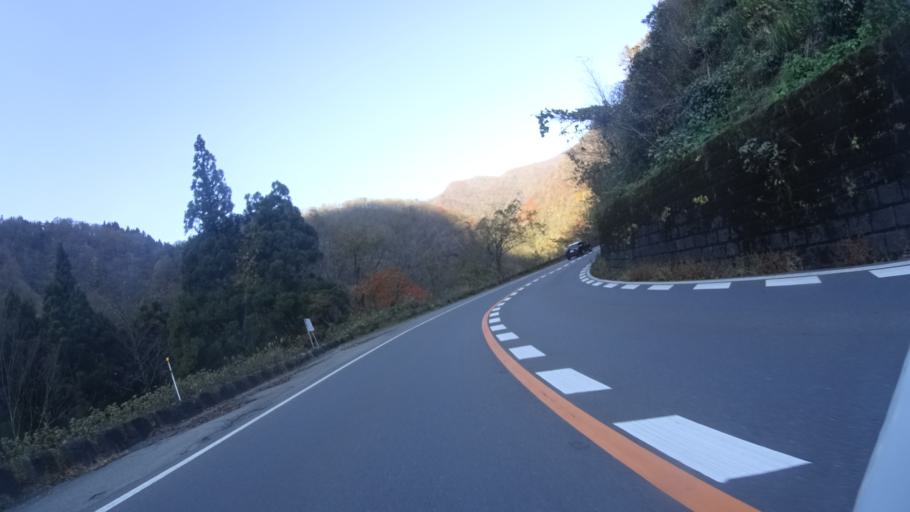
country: JP
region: Fukui
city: Ono
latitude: 35.9385
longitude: 136.6354
